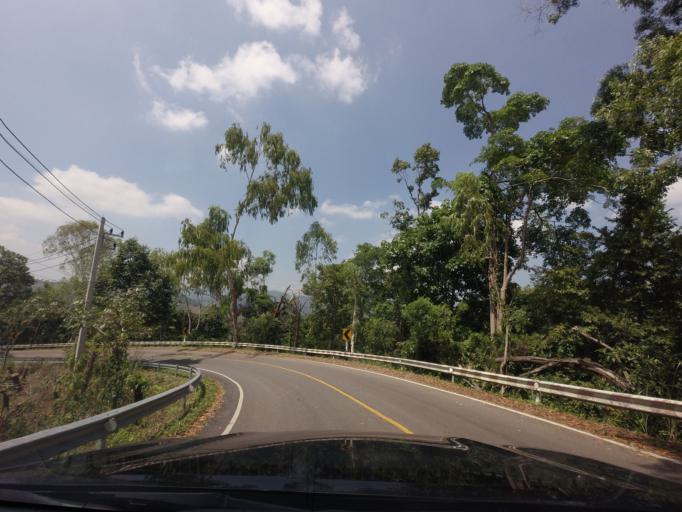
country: TH
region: Loei
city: Na Haeo
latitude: 17.4949
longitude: 100.8969
